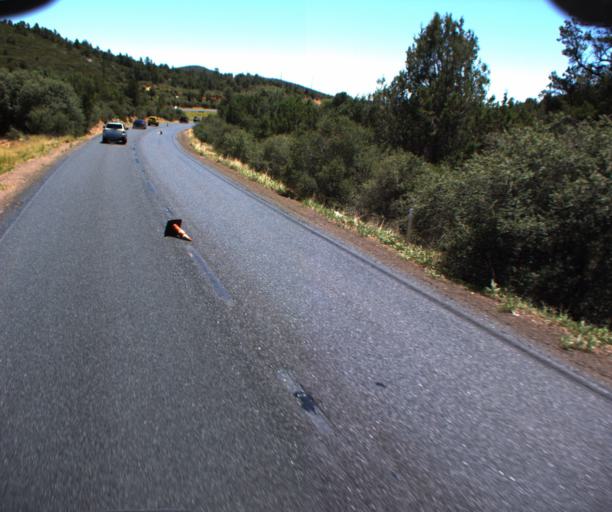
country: US
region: Arizona
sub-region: Gila County
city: Payson
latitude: 34.1967
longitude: -111.3292
